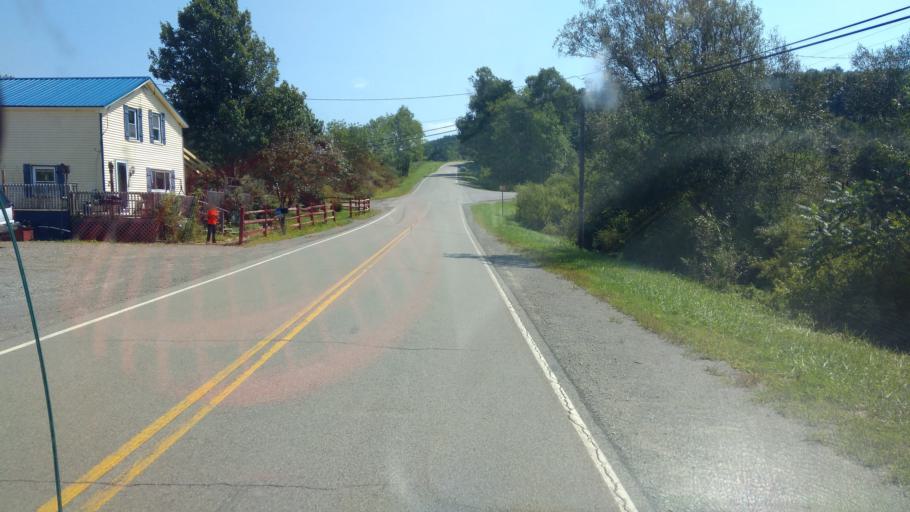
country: US
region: New York
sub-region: Allegany County
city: Belmont
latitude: 42.2925
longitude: -77.9399
